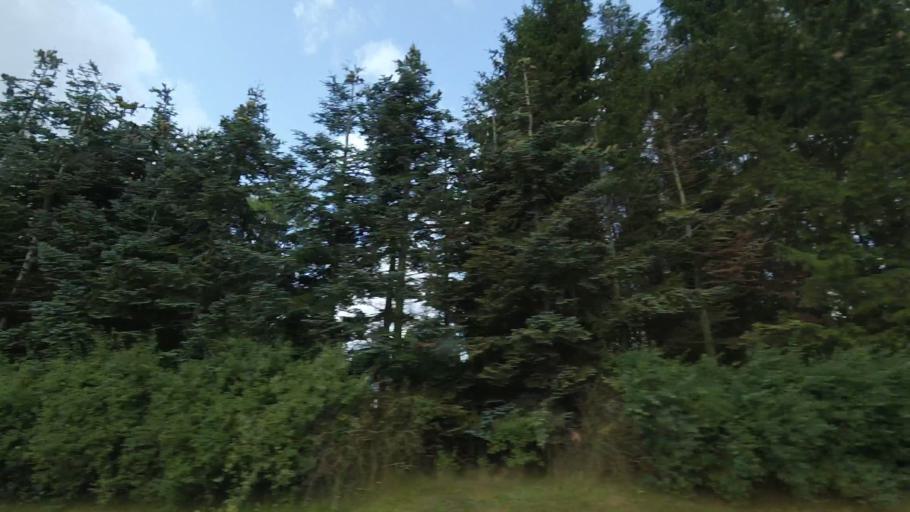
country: DK
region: Central Jutland
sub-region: Syddjurs Kommune
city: Ryomgard
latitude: 56.4211
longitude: 10.5573
